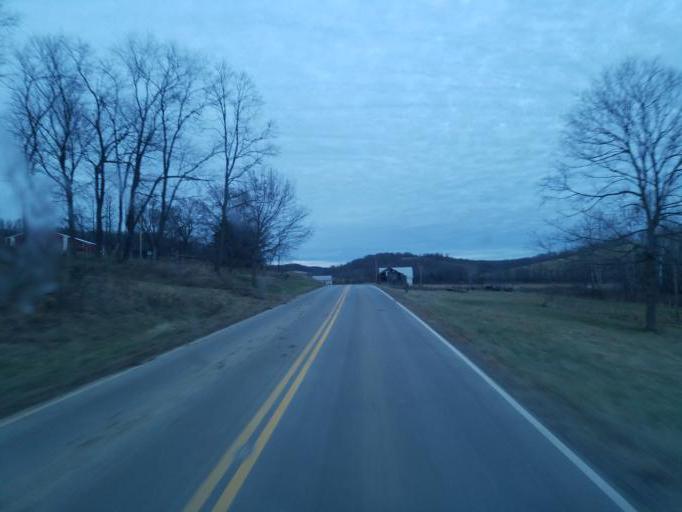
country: US
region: Ohio
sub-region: Muskingum County
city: Dresden
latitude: 40.2489
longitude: -82.0524
